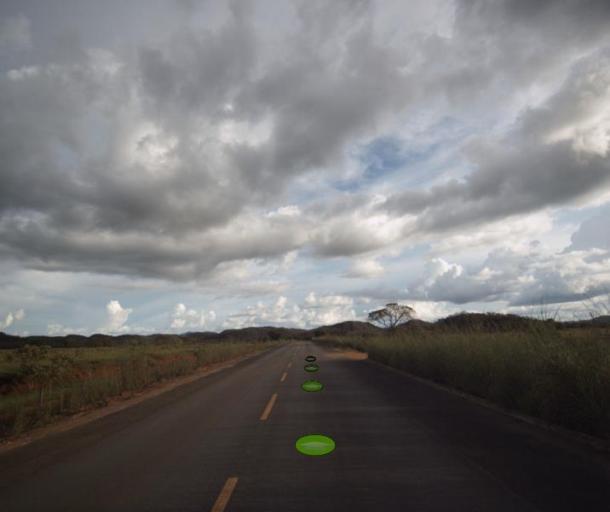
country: BR
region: Goias
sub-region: Niquelandia
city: Niquelandia
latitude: -14.5176
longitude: -48.5202
